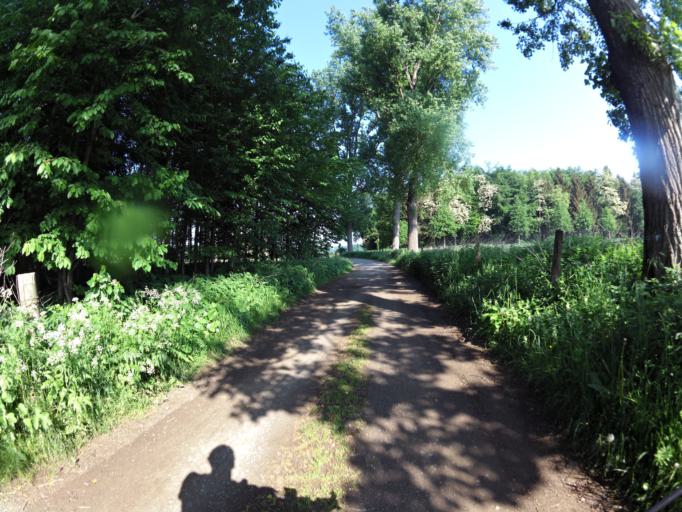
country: DE
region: North Rhine-Westphalia
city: Julich
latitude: 50.9521
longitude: 6.3232
